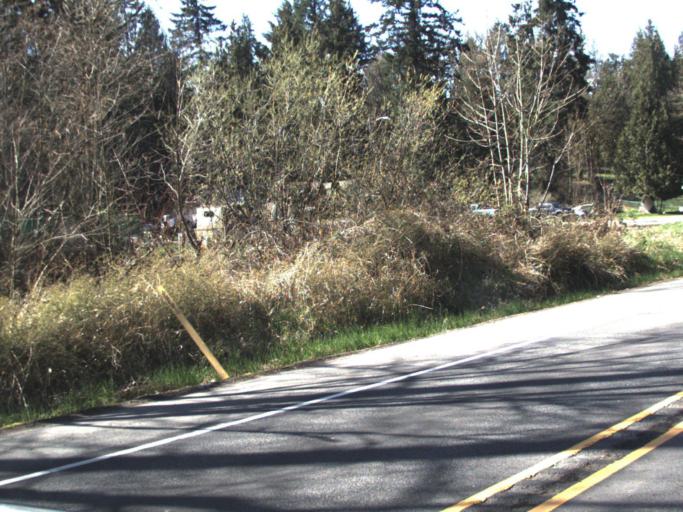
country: US
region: Washington
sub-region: King County
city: Lea Hill
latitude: 47.2704
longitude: -122.1482
